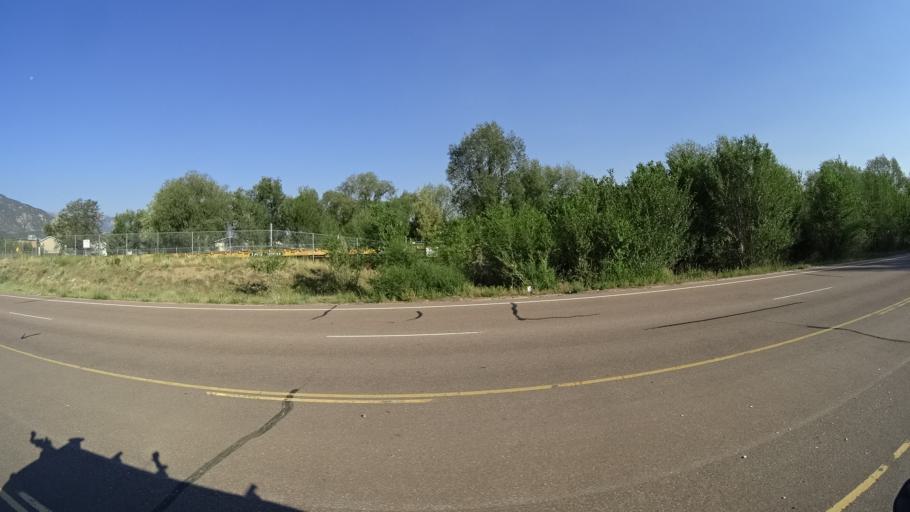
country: US
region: Colorado
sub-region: El Paso County
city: Stratmoor
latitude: 38.7727
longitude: -104.7956
